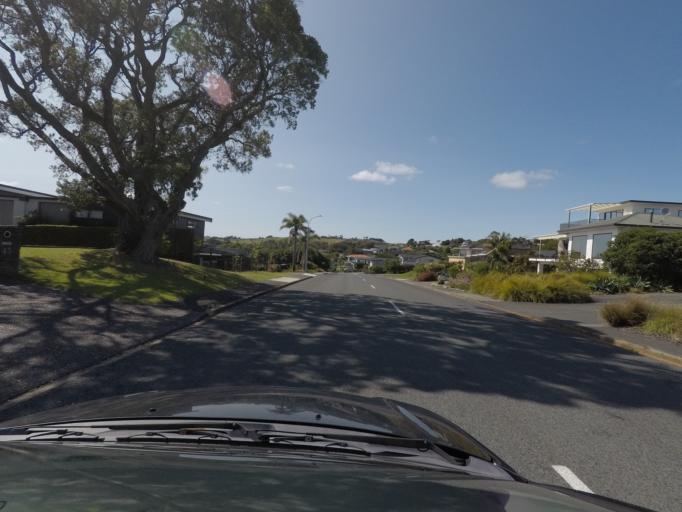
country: NZ
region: Auckland
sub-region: Auckland
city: Warkworth
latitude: -36.4314
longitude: 174.7413
